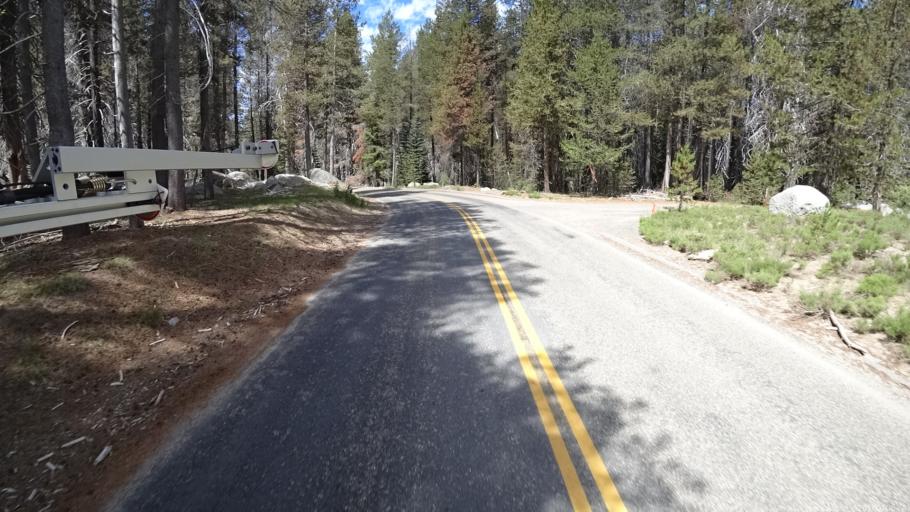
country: US
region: California
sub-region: Madera County
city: Oakhurst
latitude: 37.4548
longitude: -119.4579
